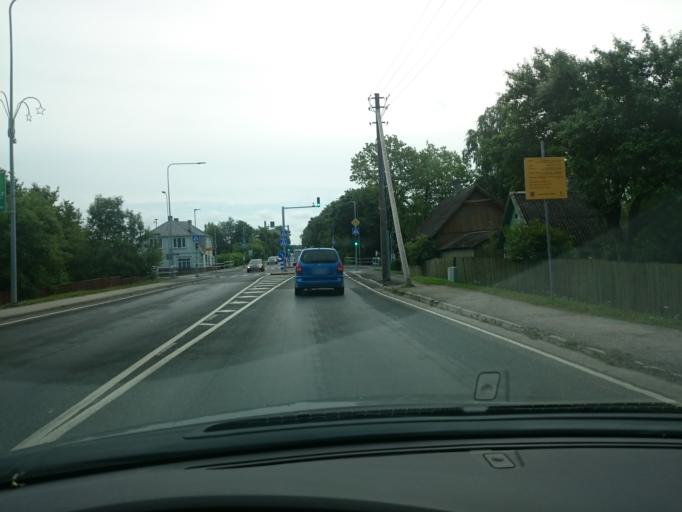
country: EE
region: Laeaene
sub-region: Haapsalu linn
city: Haapsalu
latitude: 58.9383
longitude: 23.5508
